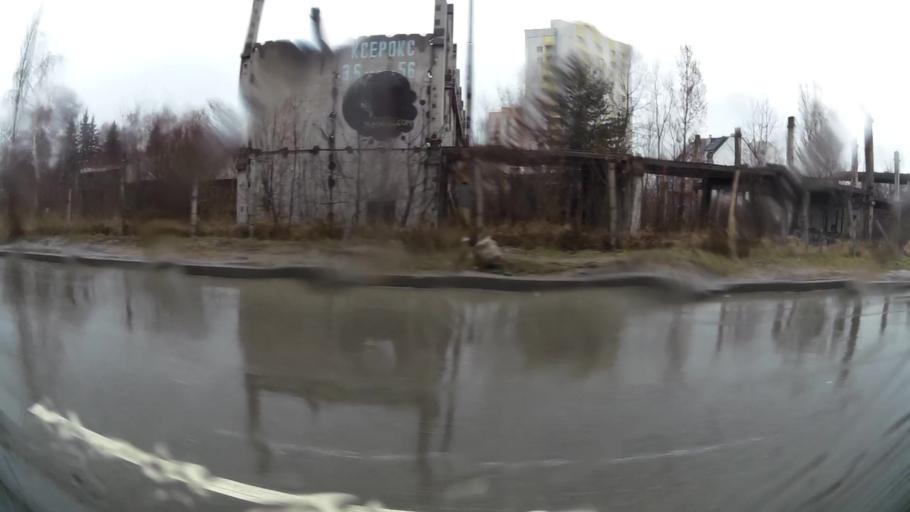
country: BG
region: Sofia-Capital
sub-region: Stolichna Obshtina
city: Sofia
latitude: 42.6470
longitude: 23.3419
